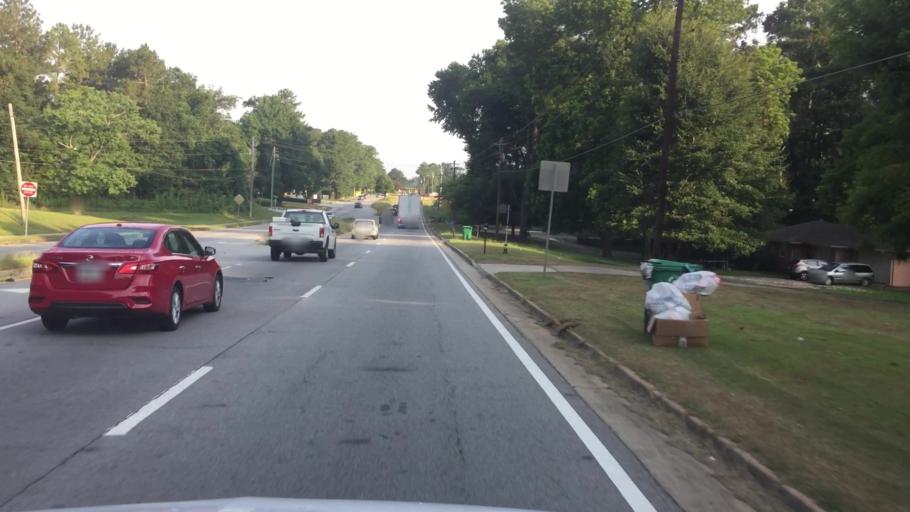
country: US
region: Georgia
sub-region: DeKalb County
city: Panthersville
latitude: 33.6871
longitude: -84.2526
